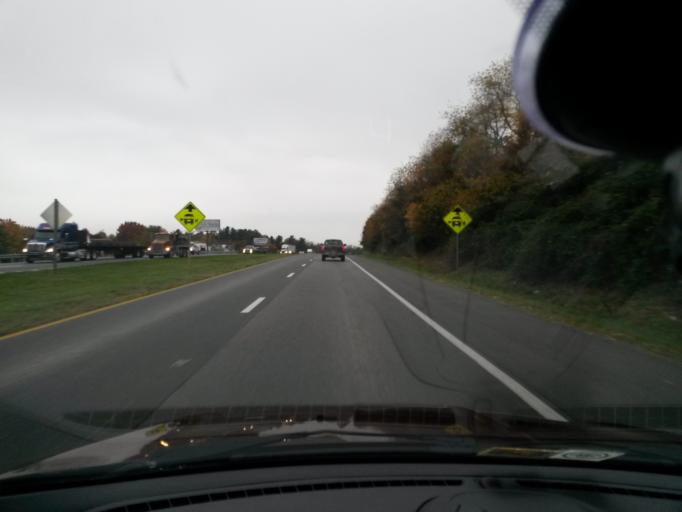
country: US
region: Virginia
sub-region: Roanoke County
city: Vinton
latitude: 37.3204
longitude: -79.8743
